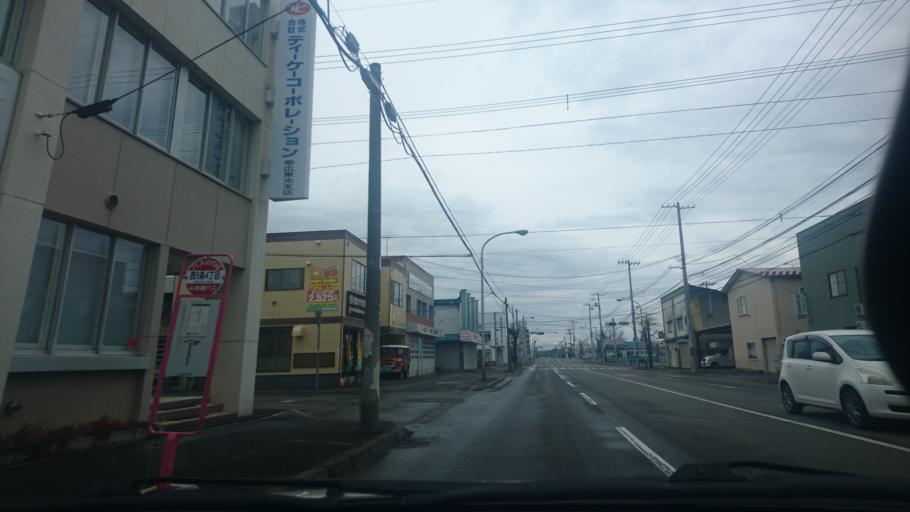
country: JP
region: Hokkaido
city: Obihiro
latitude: 42.9274
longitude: 143.1966
